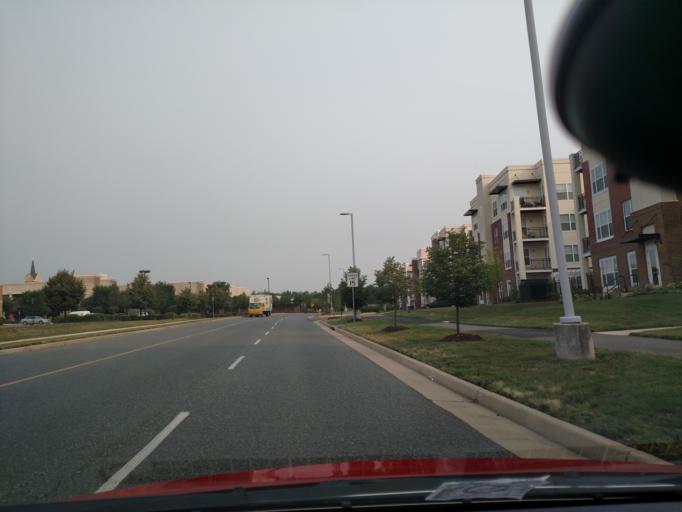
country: US
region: Virginia
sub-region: Prince William County
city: Potomac Mills
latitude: 38.6301
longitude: -77.2864
